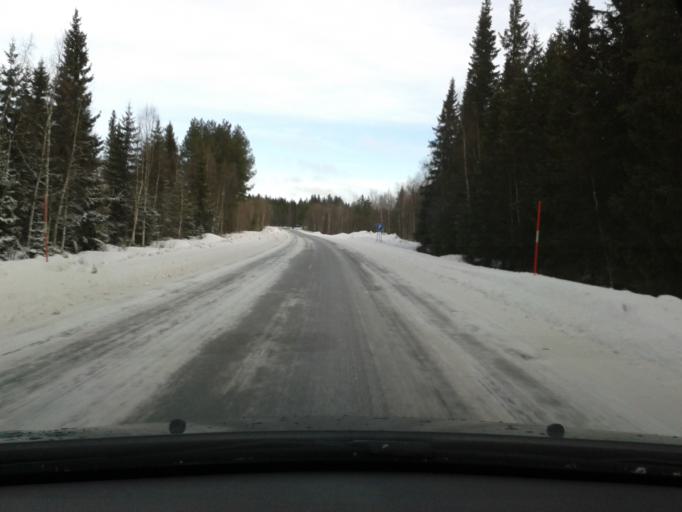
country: SE
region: Vaesterbotten
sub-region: Vilhelmina Kommun
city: Vilhelmina
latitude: 64.6456
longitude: 16.5050
